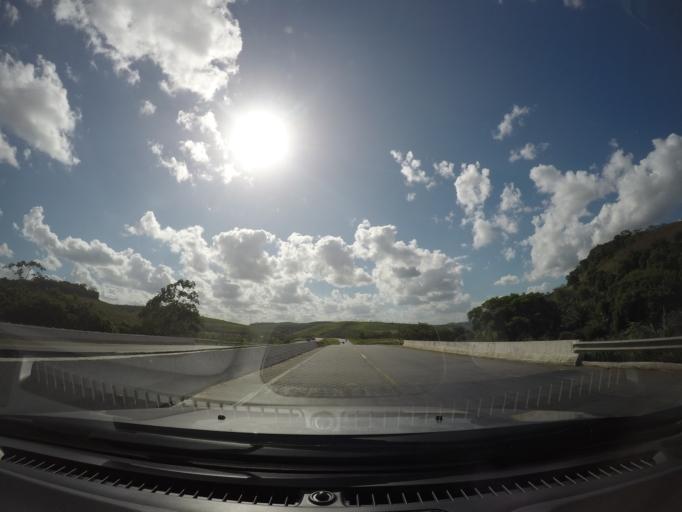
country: BR
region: Pernambuco
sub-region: Palmares
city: Palmares
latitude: -8.7614
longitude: -35.6050
